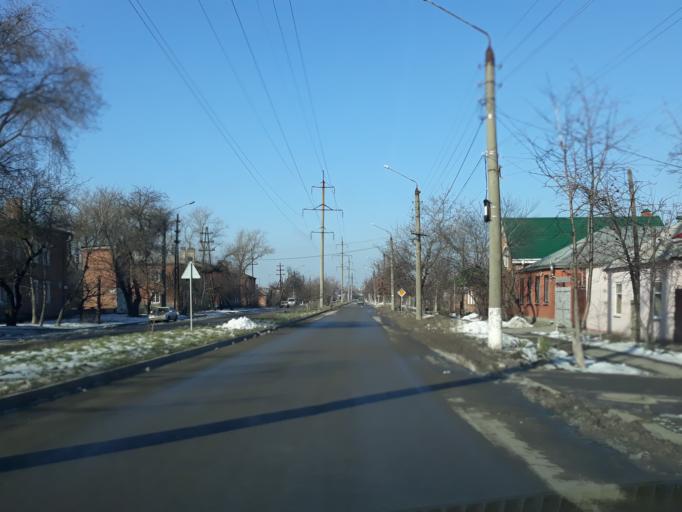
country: RU
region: Rostov
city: Taganrog
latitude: 47.2184
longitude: 38.8829
